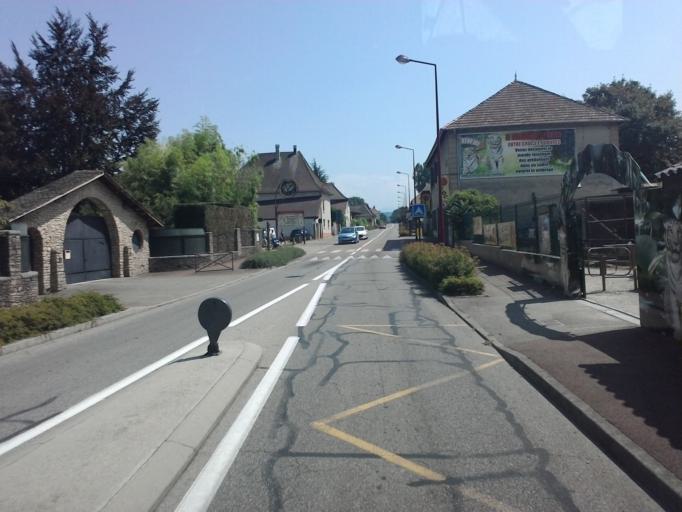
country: FR
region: Rhone-Alpes
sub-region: Departement de l'Isere
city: Fitilieu
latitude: 45.5493
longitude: 5.5758
